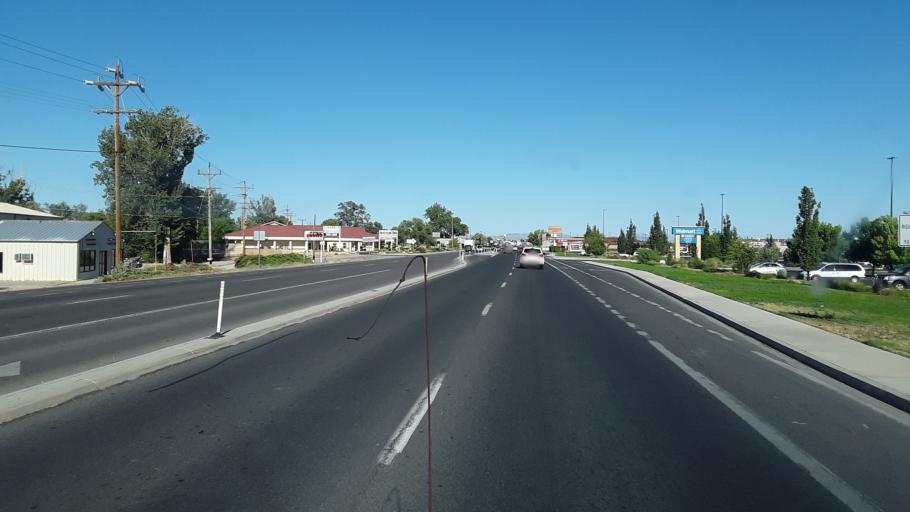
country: US
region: Nevada
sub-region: Churchill County
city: Fallon
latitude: 39.4781
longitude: -118.8078
